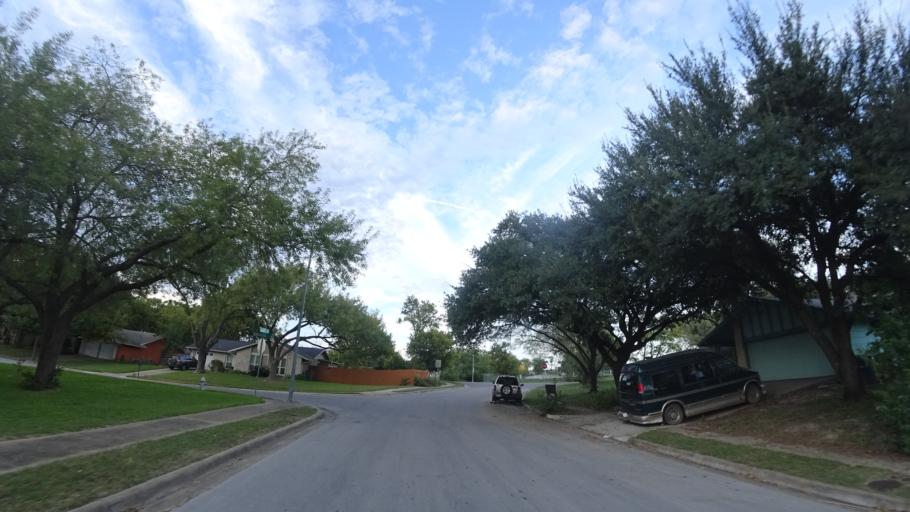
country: US
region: Texas
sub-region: Travis County
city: Austin
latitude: 30.2067
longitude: -97.7627
